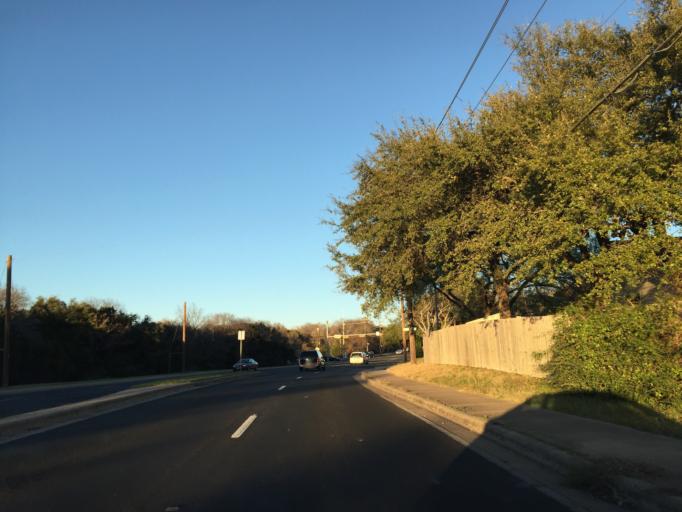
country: US
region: Texas
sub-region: Williamson County
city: Jollyville
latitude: 30.4310
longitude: -97.7797
